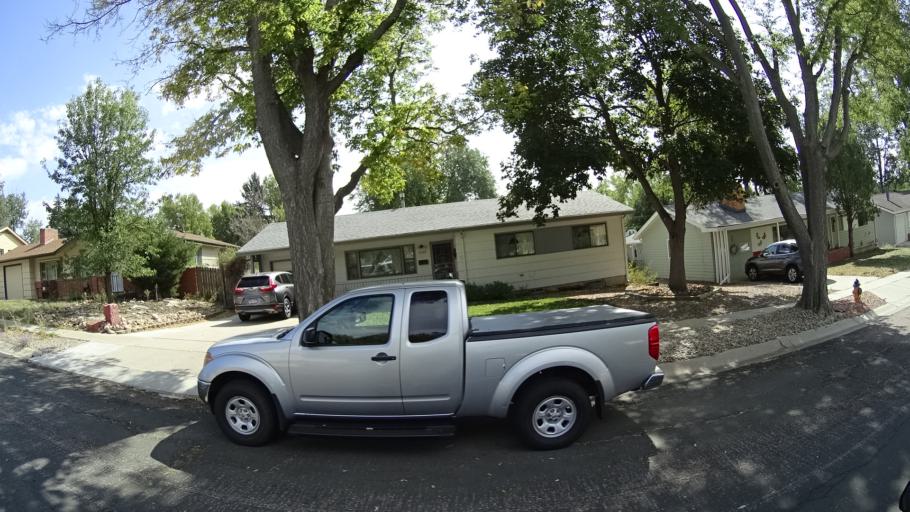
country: US
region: Colorado
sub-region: El Paso County
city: Colorado Springs
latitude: 38.8642
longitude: -104.7736
